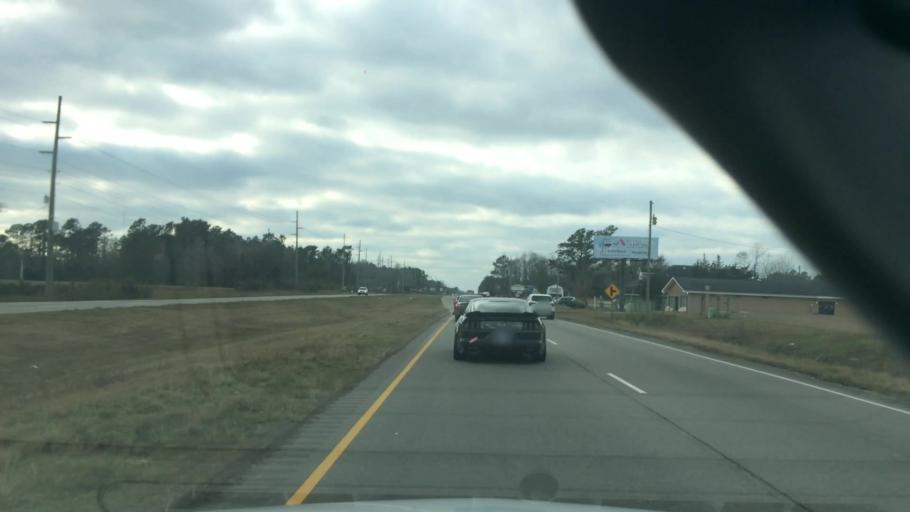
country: US
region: North Carolina
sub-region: Brunswick County
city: Shallotte
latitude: 34.0082
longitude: -78.2989
